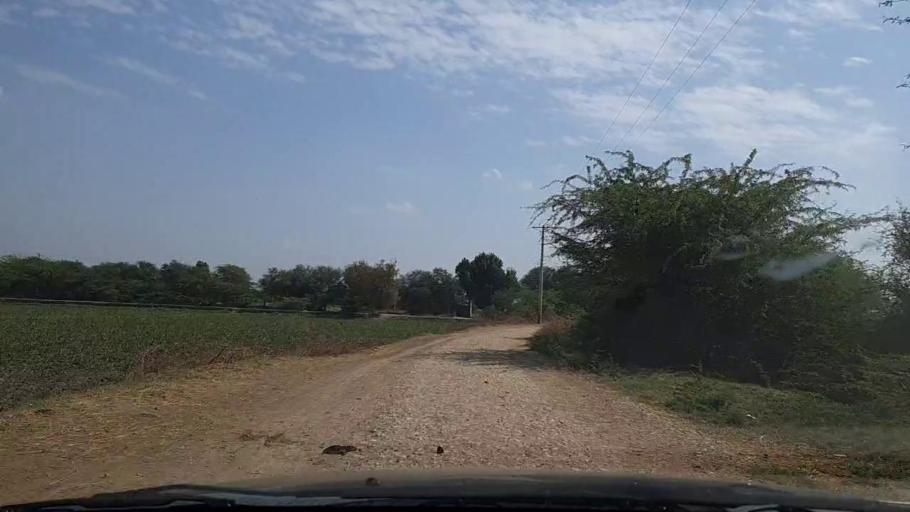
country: PK
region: Sindh
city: Mirpur Batoro
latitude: 24.5624
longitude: 68.2012
